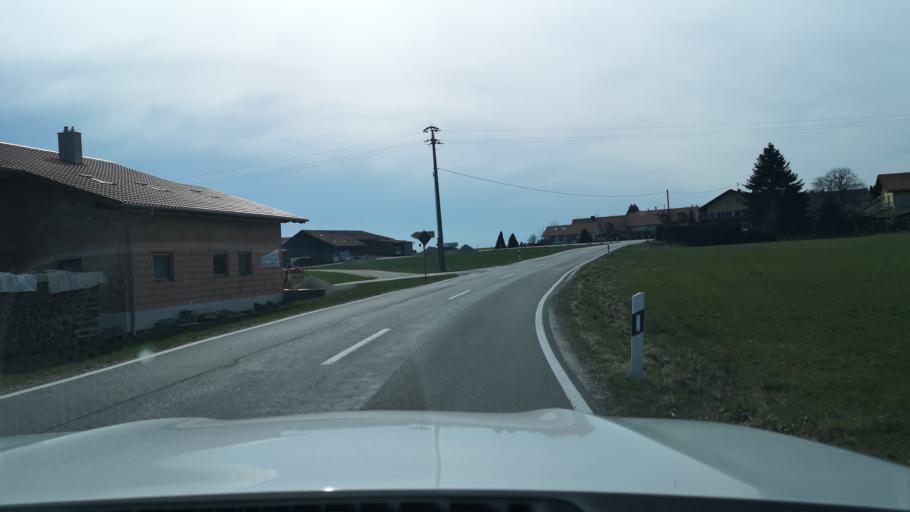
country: DE
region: Bavaria
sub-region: Upper Bavaria
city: Hohenlinden
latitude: 48.1691
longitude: 12.0320
